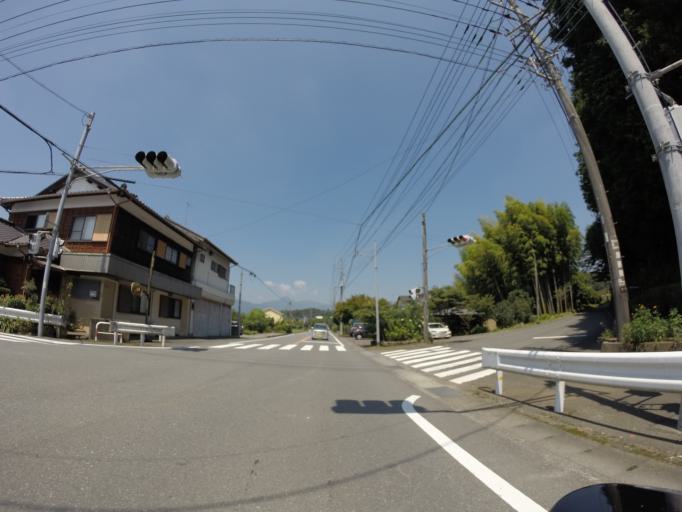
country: JP
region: Shizuoka
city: Fujinomiya
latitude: 35.2709
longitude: 138.6194
